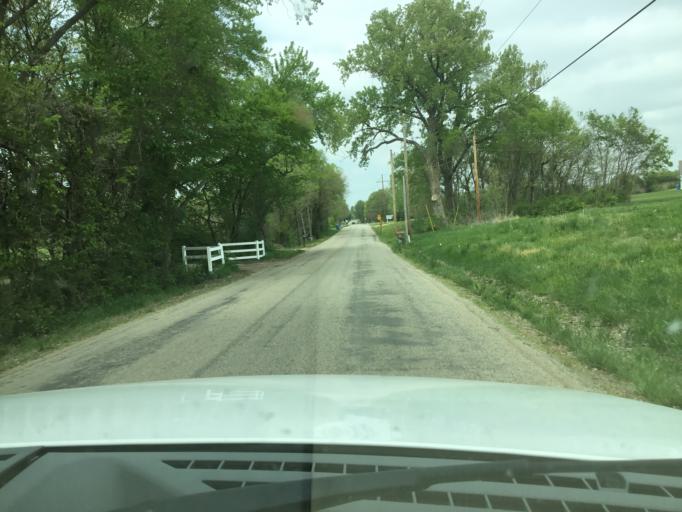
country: US
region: Kansas
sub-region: Shawnee County
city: Topeka
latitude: 39.0119
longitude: -95.5861
